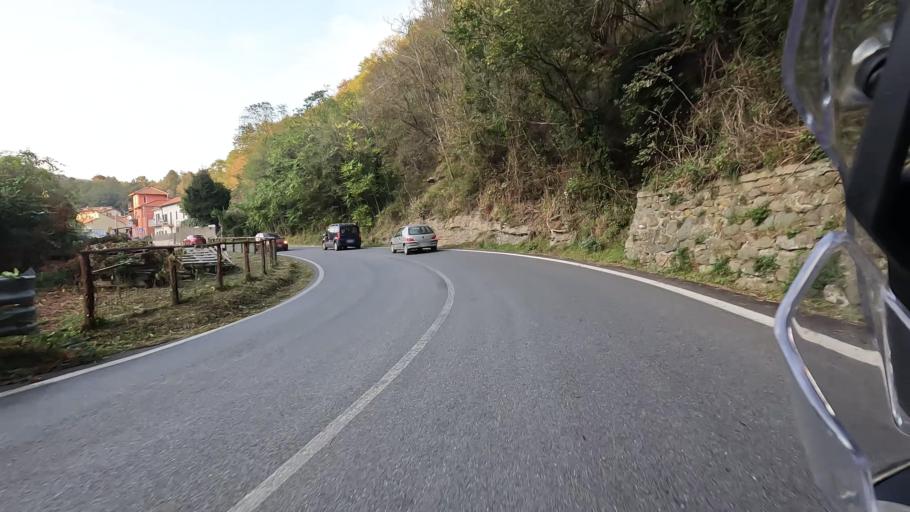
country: IT
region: Liguria
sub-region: Provincia di Savona
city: Osteria dei Cacciatori-Stella
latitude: 44.4152
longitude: 8.4833
